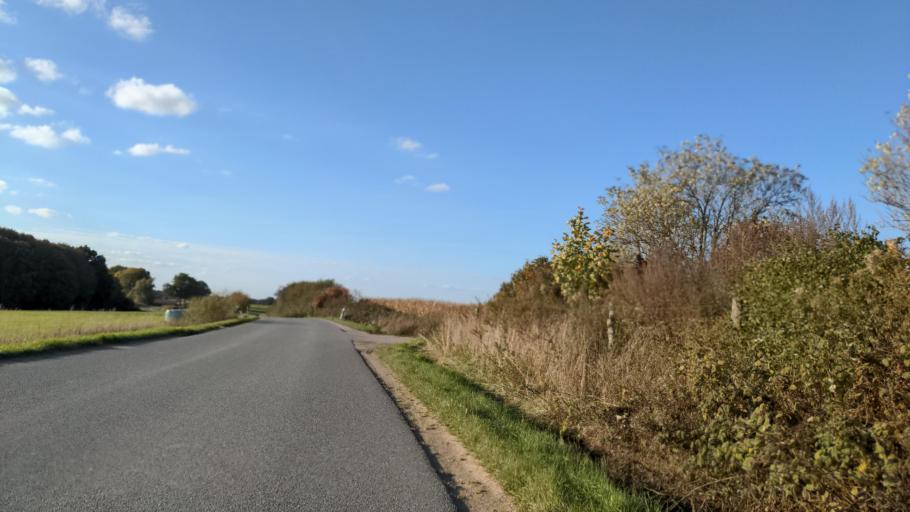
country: DE
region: Schleswig-Holstein
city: Pronstorf
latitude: 53.9599
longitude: 10.5207
